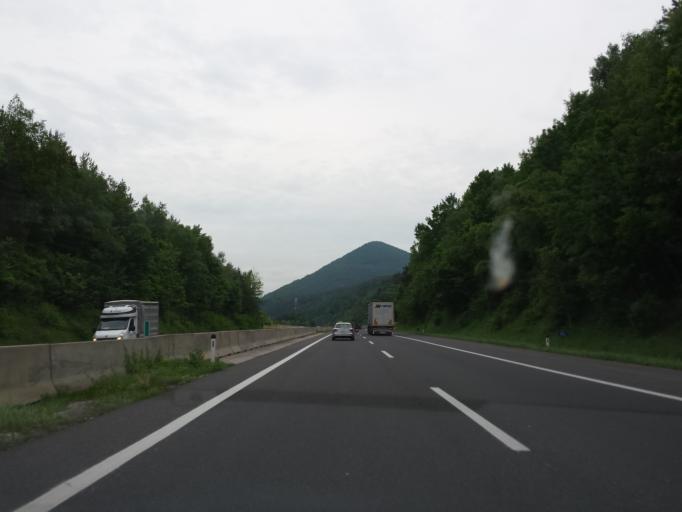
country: AT
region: Lower Austria
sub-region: Politischer Bezirk Neunkirchen
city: Warth
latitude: 47.6563
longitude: 16.1241
